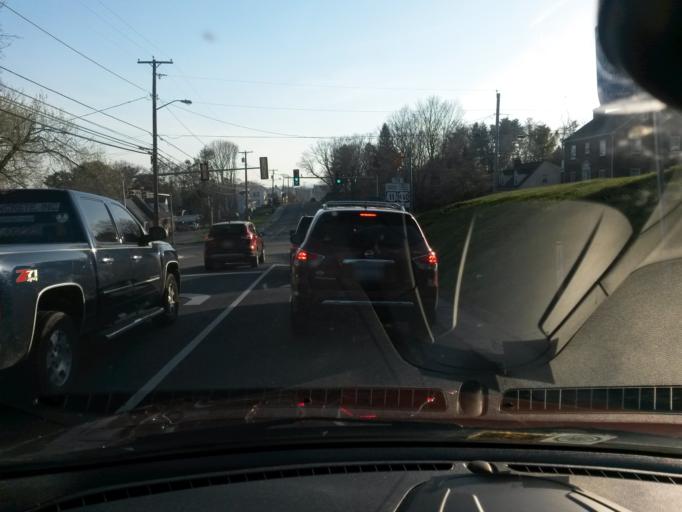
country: US
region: Virginia
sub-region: Montgomery County
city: Christiansburg
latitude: 37.1236
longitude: -80.4159
